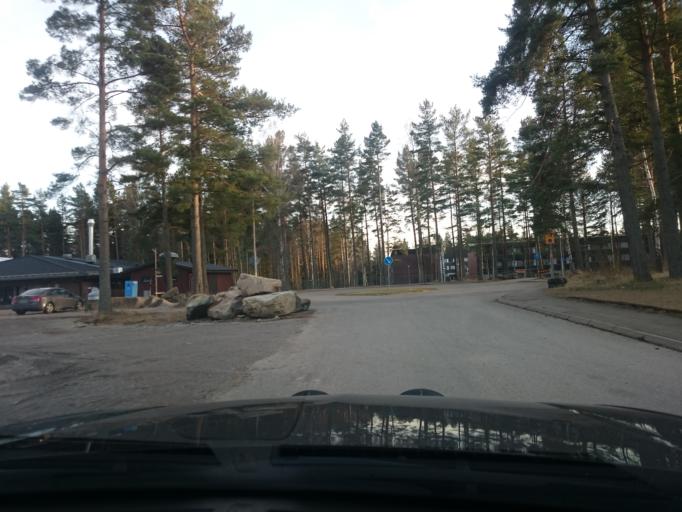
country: SE
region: Joenkoeping
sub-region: Vetlanda Kommun
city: Vetlanda
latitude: 57.4174
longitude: 15.0971
